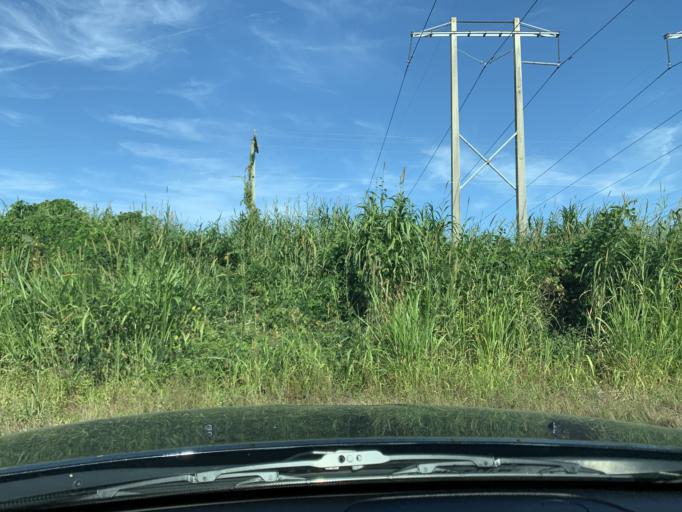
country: US
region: Florida
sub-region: Miami-Dade County
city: Three Lakes
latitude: 25.6414
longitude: -80.3960
